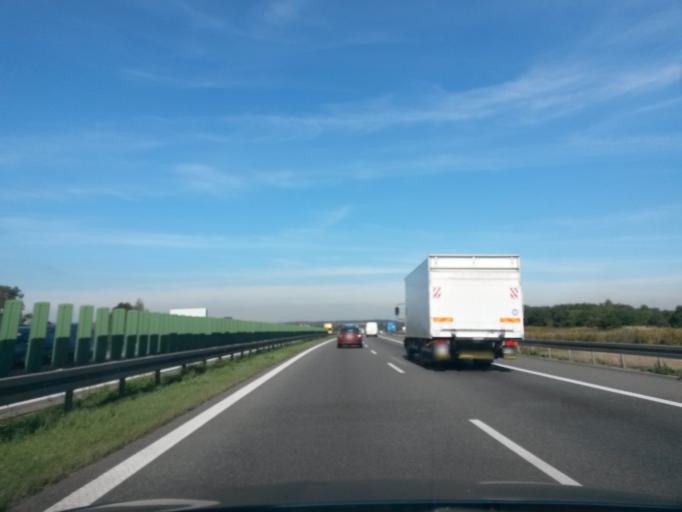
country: PL
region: Lesser Poland Voivodeship
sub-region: Powiat krakowski
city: Kryspinow
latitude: 50.0622
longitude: 19.8096
